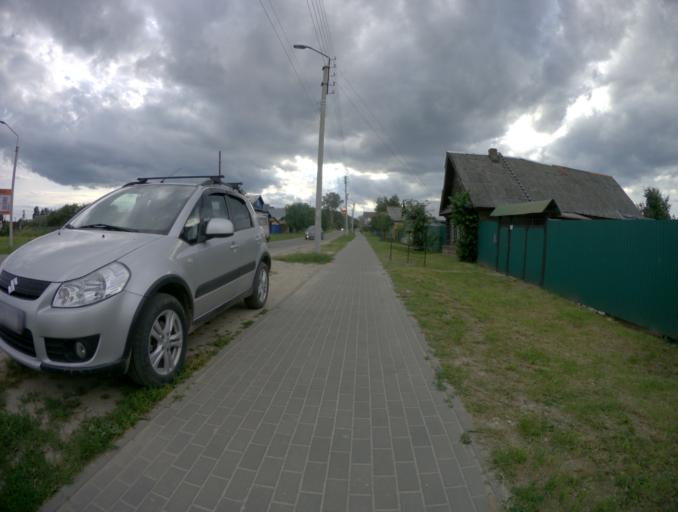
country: RU
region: Vladimir
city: Gorokhovets
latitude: 56.2014
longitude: 42.7024
